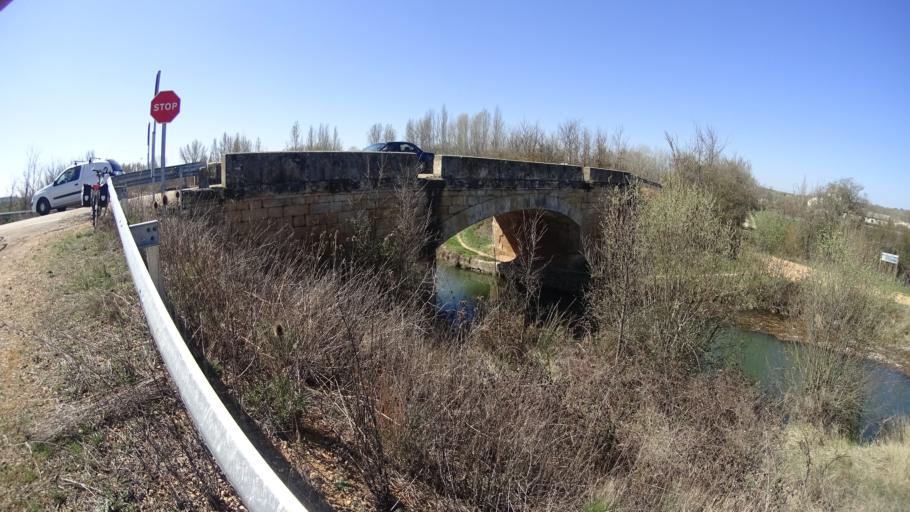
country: ES
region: Castille and Leon
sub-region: Provincia de Palencia
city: Herrera de Pisuerga
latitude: 42.5996
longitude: -4.3147
